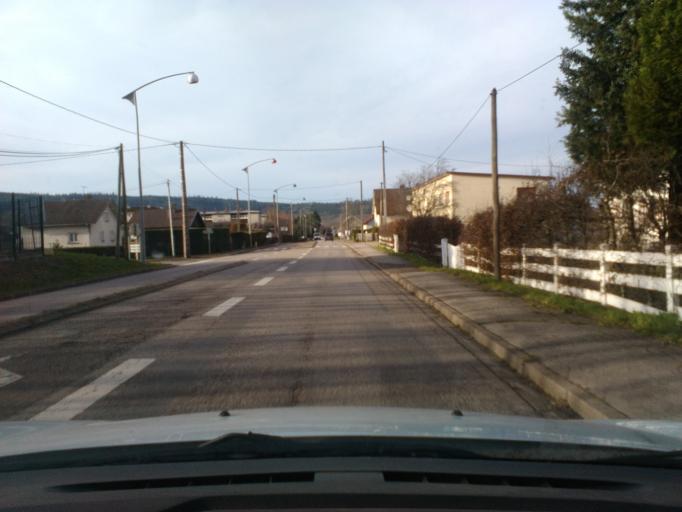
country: FR
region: Lorraine
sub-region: Departement des Vosges
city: Anould
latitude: 48.1856
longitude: 6.9598
